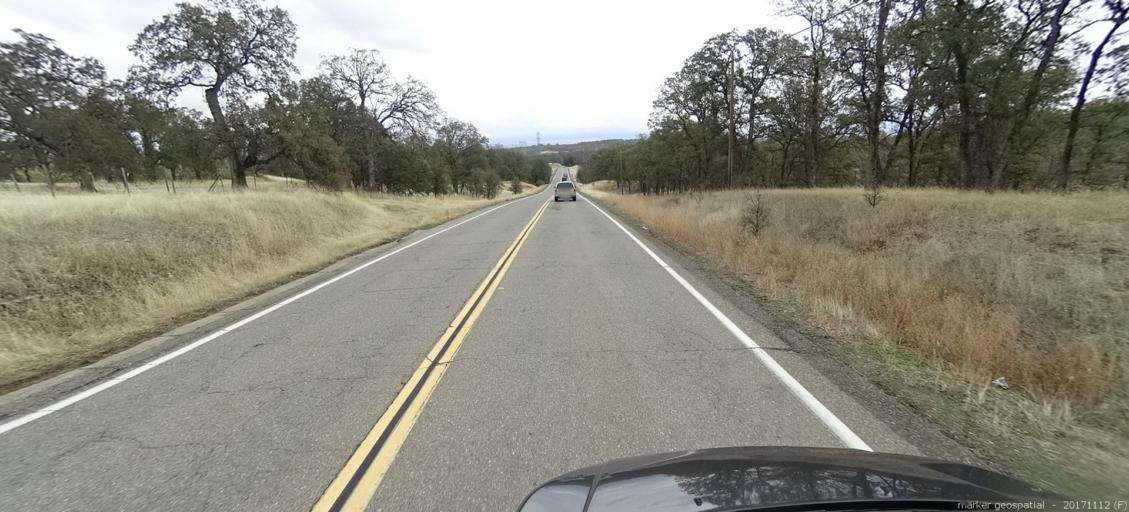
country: US
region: California
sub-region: Shasta County
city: Palo Cedro
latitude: 40.4784
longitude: -122.2130
